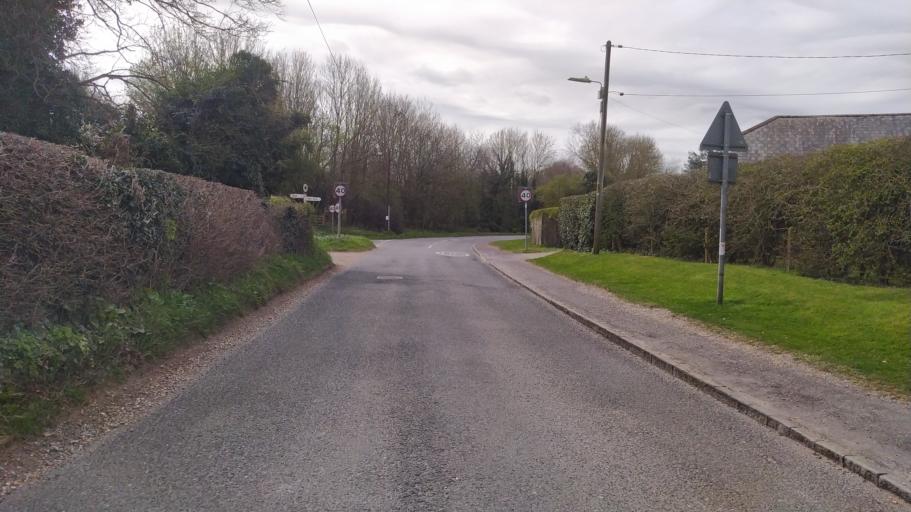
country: GB
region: England
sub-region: Hampshire
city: Bishops Waltham
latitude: 50.9638
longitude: -1.2081
